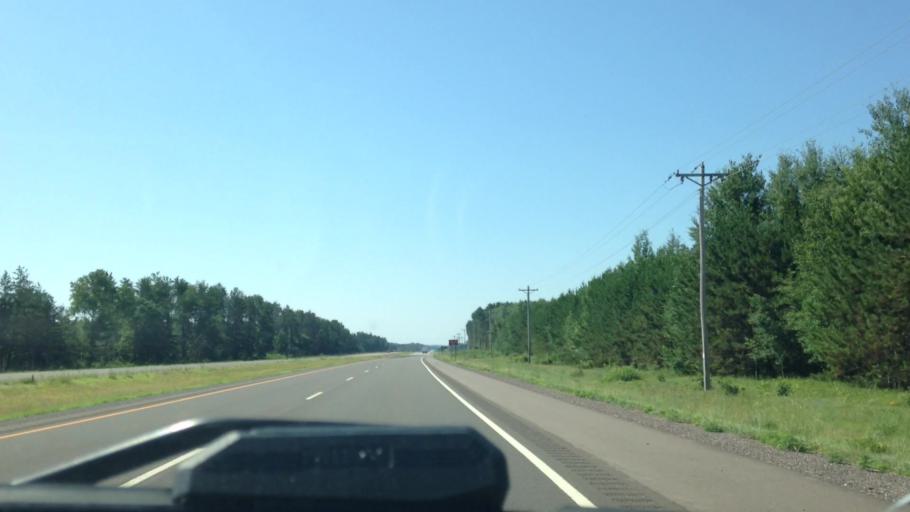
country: US
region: Wisconsin
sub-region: Washburn County
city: Spooner
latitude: 45.9277
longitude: -91.8279
